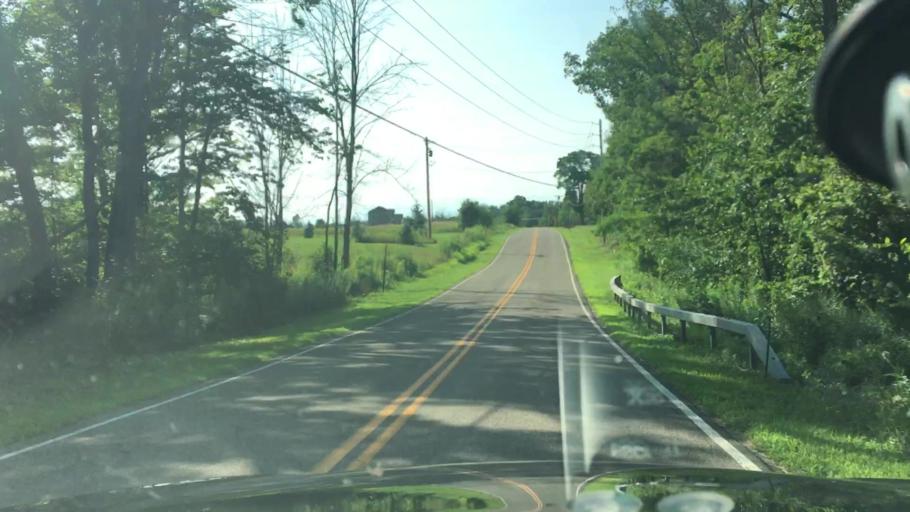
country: US
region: New York
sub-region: Erie County
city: North Collins
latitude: 42.6276
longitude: -78.9764
